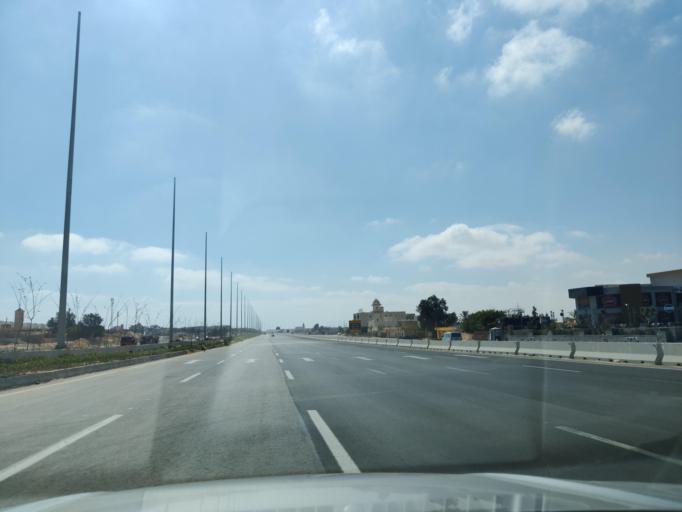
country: EG
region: Muhafazat Matruh
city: Al `Alamayn
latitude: 30.9908
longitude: 28.6814
